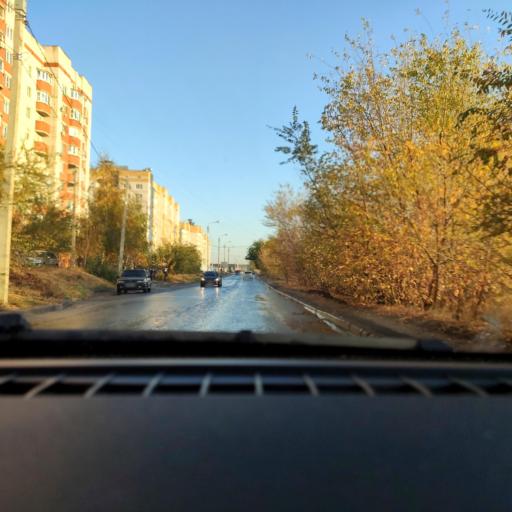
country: RU
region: Voronezj
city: Somovo
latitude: 51.6716
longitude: 39.2909
